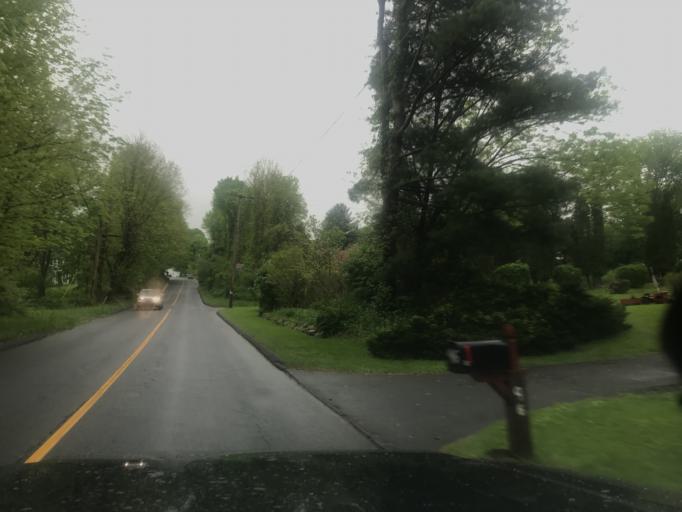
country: US
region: Connecticut
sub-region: Fairfield County
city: Bethel
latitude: 41.3927
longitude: -73.3839
